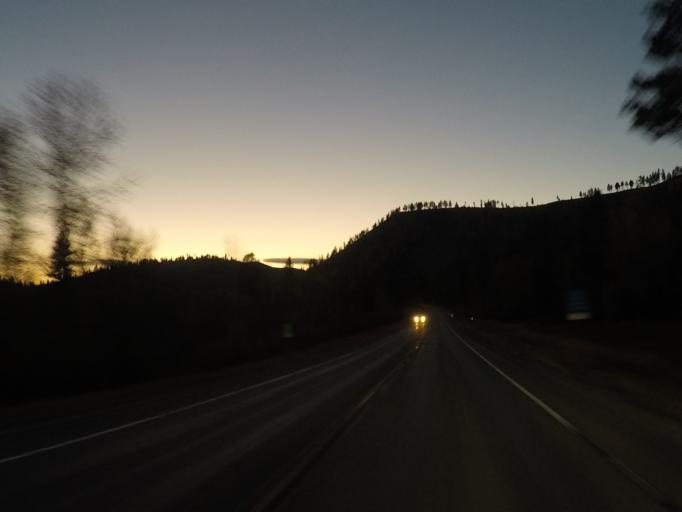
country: US
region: Montana
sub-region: Missoula County
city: Seeley Lake
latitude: 47.0229
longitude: -113.2963
